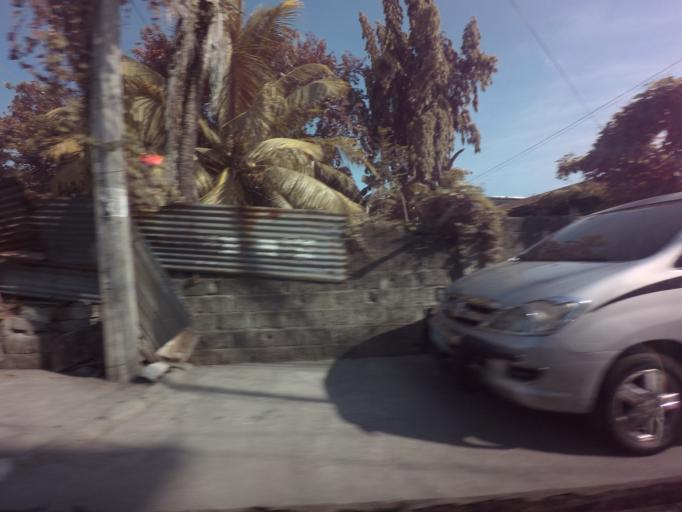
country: PH
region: Calabarzon
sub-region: Province of Rizal
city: Taguig
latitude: 14.4963
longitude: 121.0564
